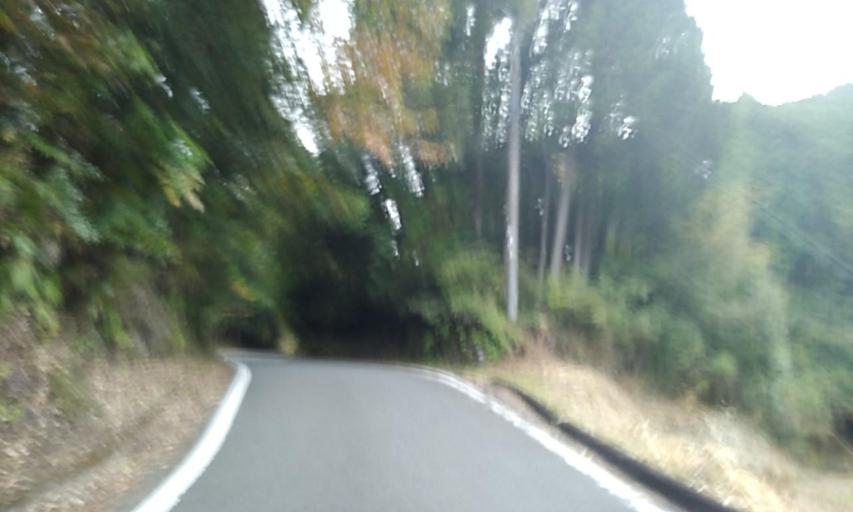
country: JP
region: Wakayama
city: Shingu
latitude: 33.9324
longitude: 135.9727
